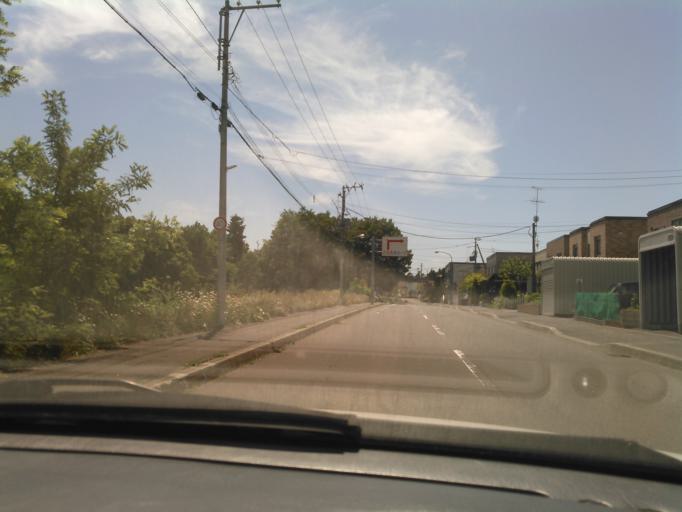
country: JP
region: Hokkaido
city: Ebetsu
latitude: 43.0801
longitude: 141.5241
